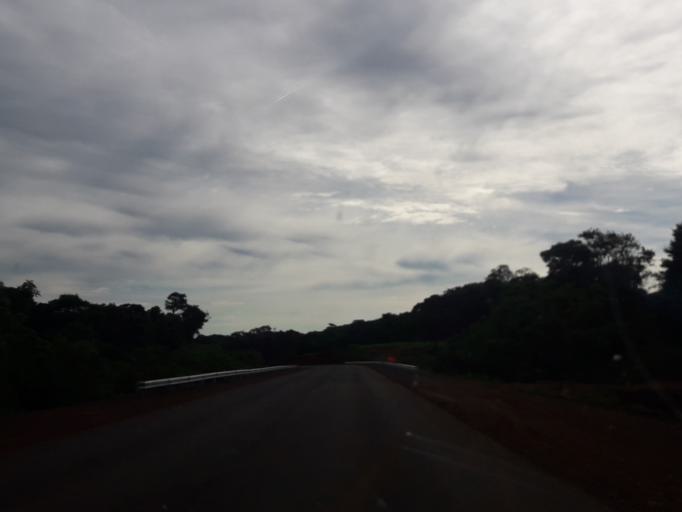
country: AR
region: Misiones
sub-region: Departamento de San Pedro
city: San Pedro
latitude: -26.5101
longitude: -53.9035
